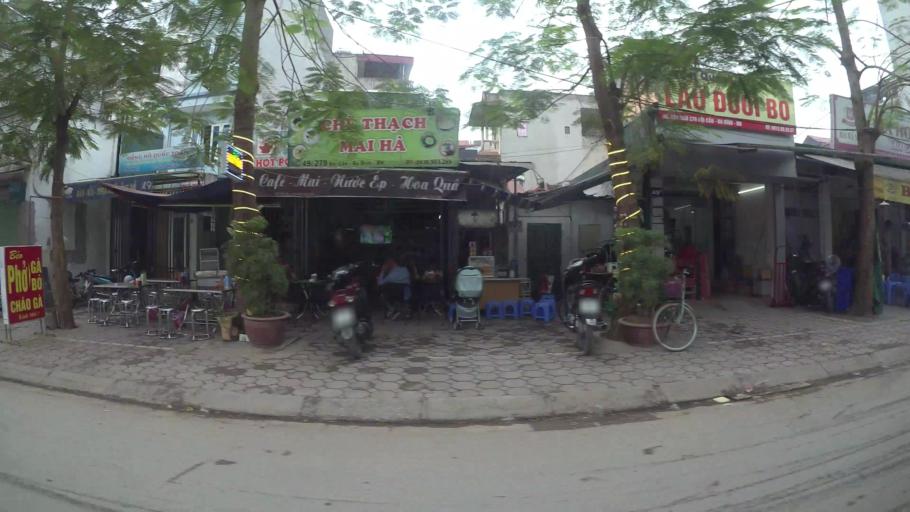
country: VN
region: Ha Noi
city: Cau Giay
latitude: 21.0380
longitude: 105.8205
